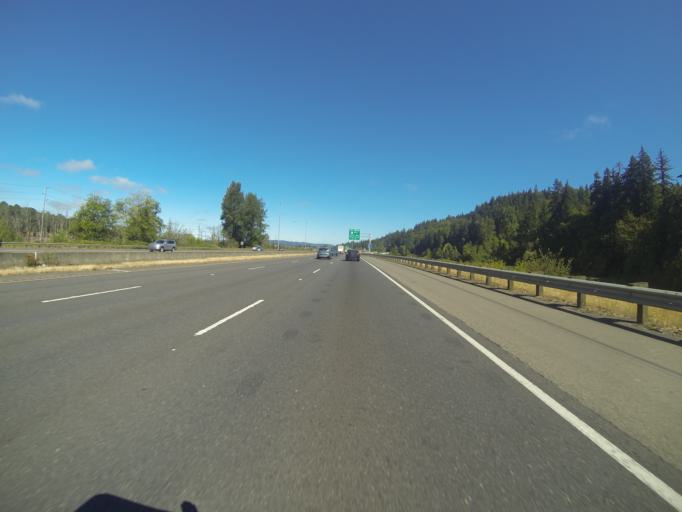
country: US
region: Washington
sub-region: Cowlitz County
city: Kelso
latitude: 46.0964
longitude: -122.8730
